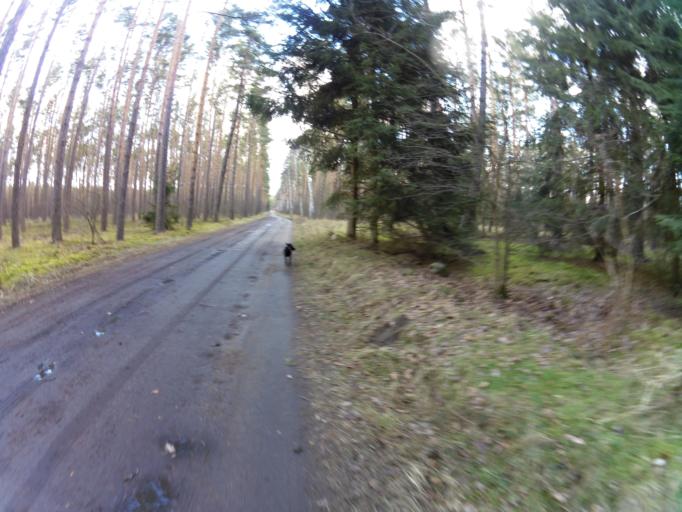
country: PL
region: West Pomeranian Voivodeship
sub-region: Powiat mysliborski
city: Debno
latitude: 52.7905
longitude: 14.7486
